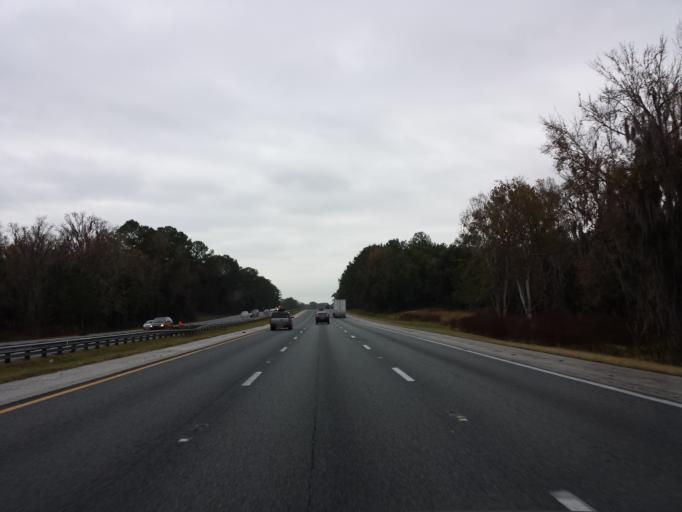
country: US
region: Florida
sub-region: Alachua County
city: Gainesville
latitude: 29.5341
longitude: -82.3209
